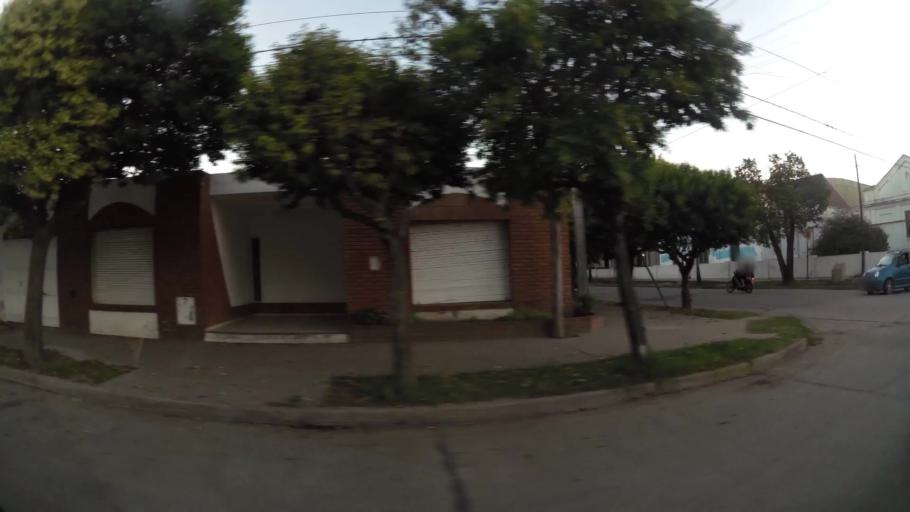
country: AR
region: Cordoba
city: Villa Maria
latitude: -32.4107
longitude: -63.2589
